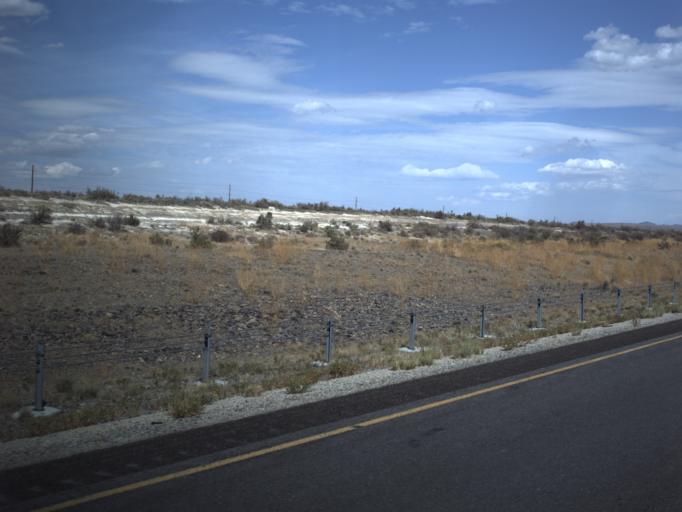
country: US
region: Utah
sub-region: Tooele County
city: Grantsville
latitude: 40.7261
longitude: -113.1339
